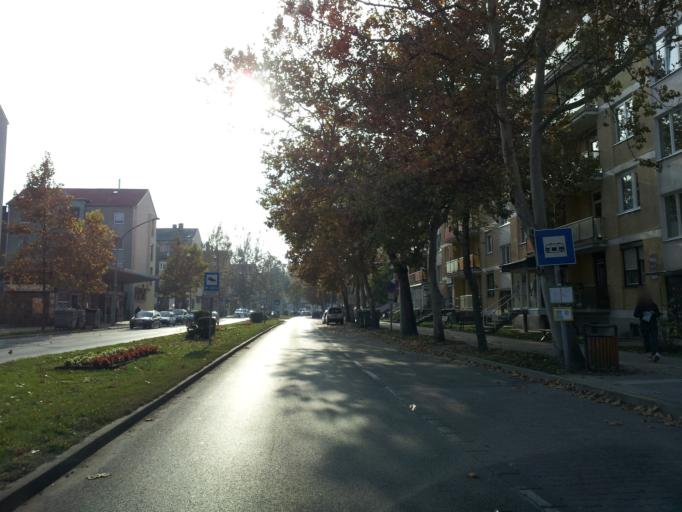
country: HU
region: Komarom-Esztergom
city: Oroszlany
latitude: 47.4864
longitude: 18.3140
